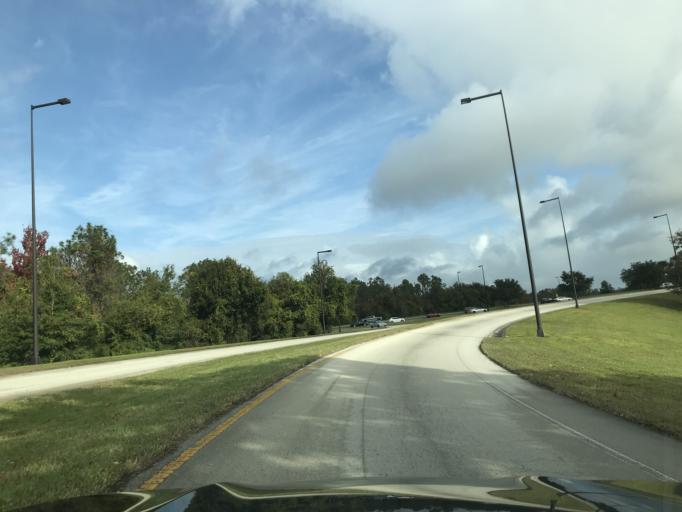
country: US
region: Florida
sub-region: Osceola County
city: Celebration
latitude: 28.3620
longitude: -81.5667
